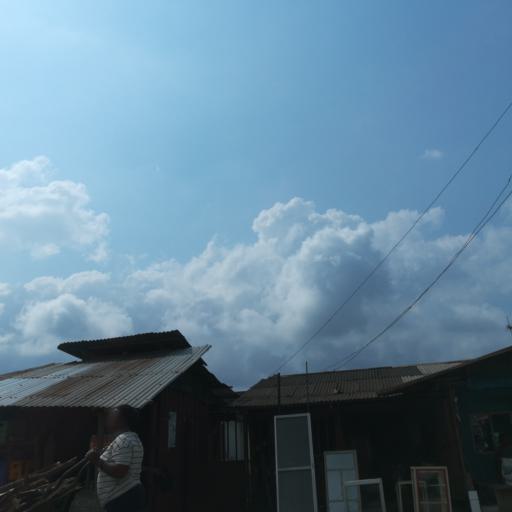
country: NG
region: Rivers
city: Okrika
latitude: 4.7931
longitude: 7.1178
